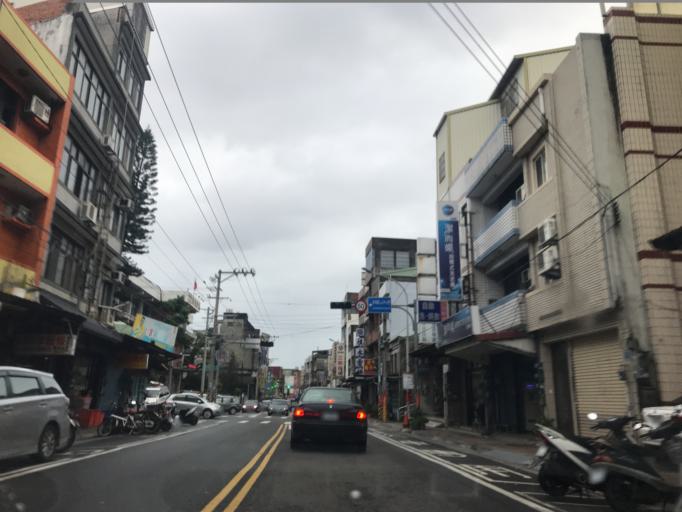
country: TW
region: Taiwan
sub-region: Hsinchu
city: Zhubei
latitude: 24.8280
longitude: 121.0751
